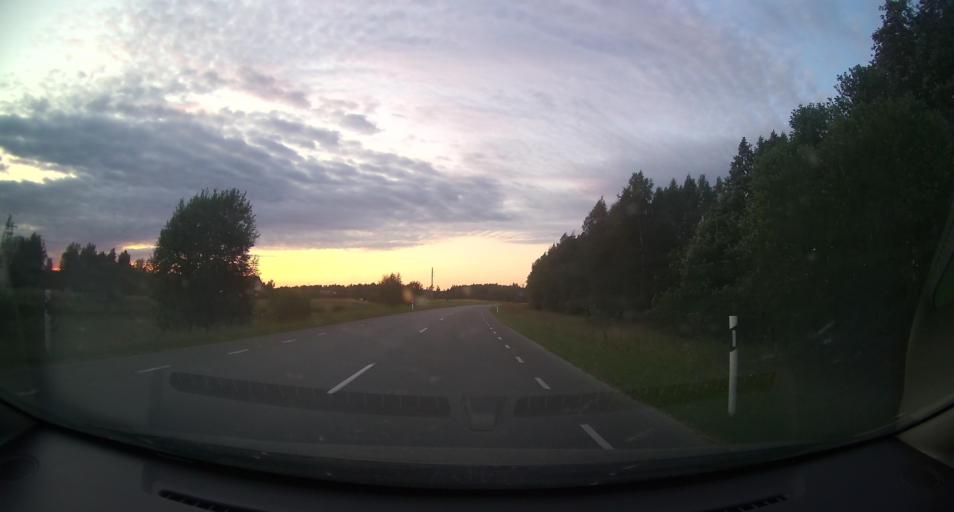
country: EE
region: Harju
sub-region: Raasiku vald
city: Raasiku
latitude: 59.2010
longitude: 25.1813
